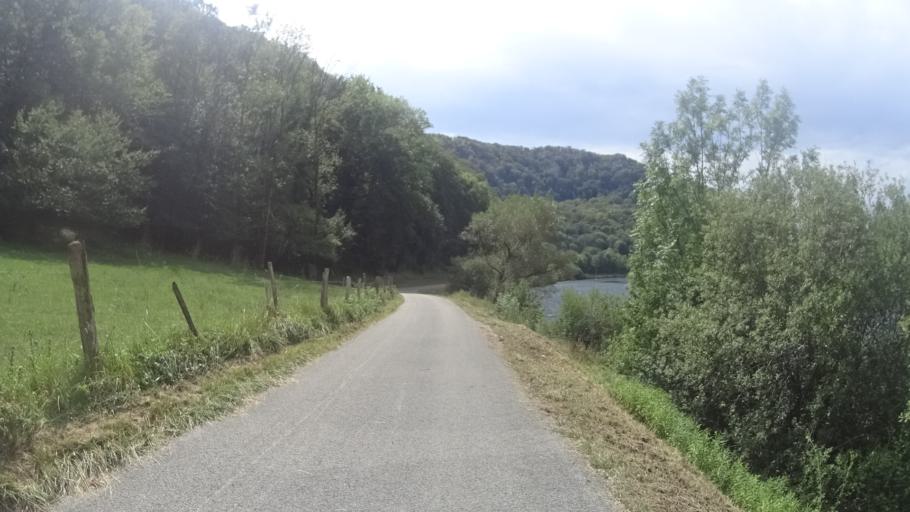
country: FR
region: Franche-Comte
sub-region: Departement du Doubs
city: Baume-les-Dames
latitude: 47.3550
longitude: 6.3921
